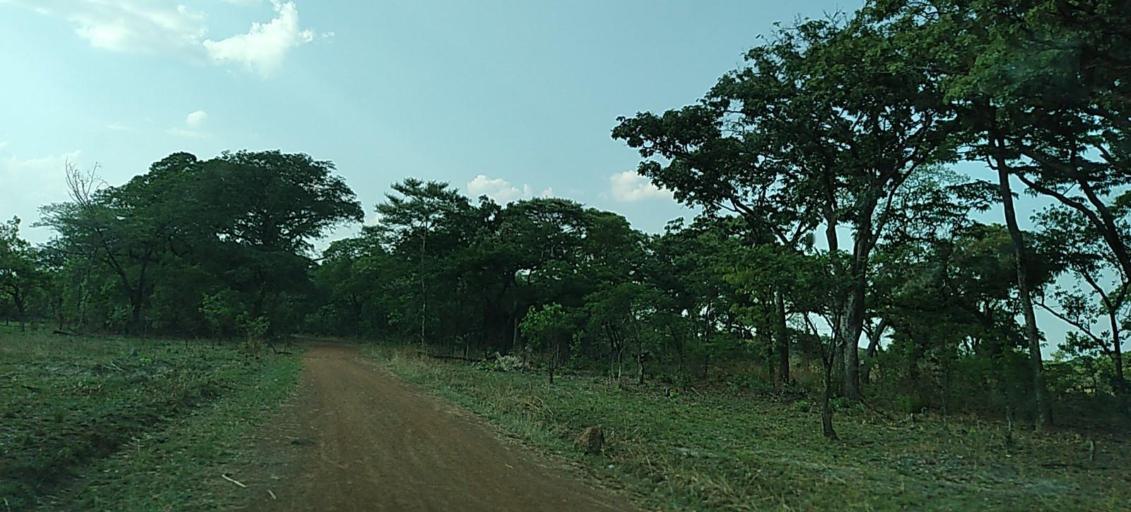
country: ZM
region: Copperbelt
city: Mpongwe
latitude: -13.4347
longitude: 28.0585
